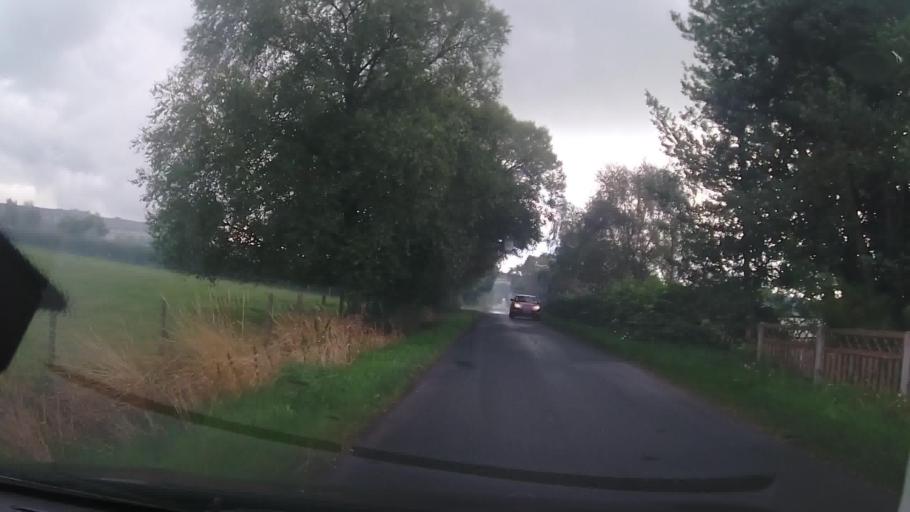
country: GB
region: England
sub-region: Shropshire
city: Norbury
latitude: 52.5816
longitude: -2.9551
